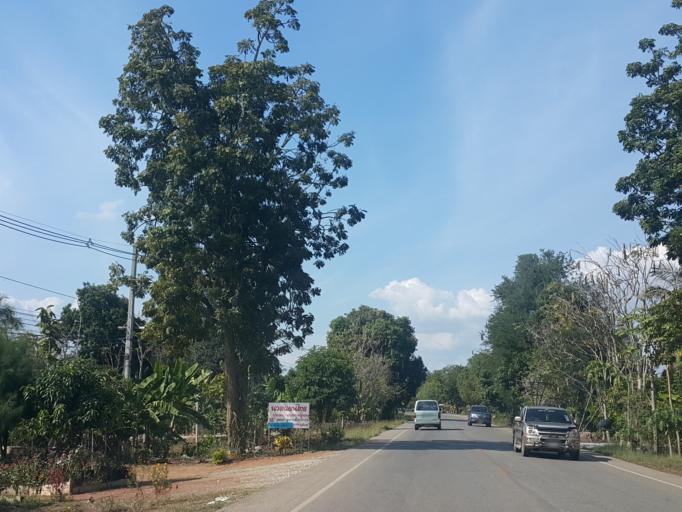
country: TH
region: Sukhothai
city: Sawankhalok
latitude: 17.2658
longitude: 99.8344
